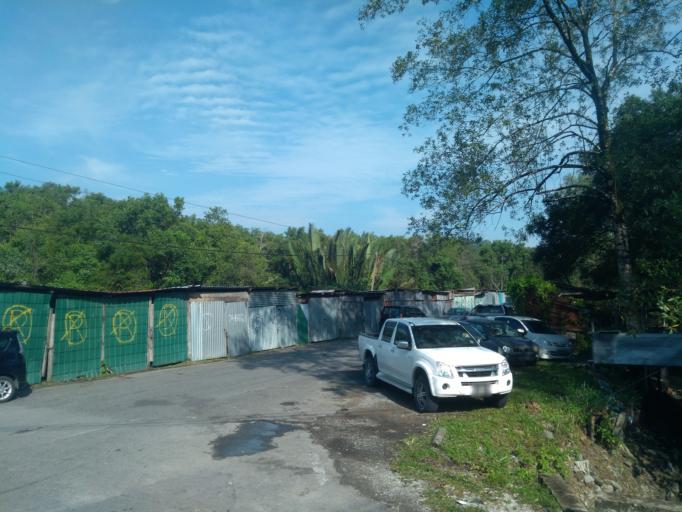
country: MY
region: Sarawak
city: Kuching
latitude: 1.6617
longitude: 110.4315
